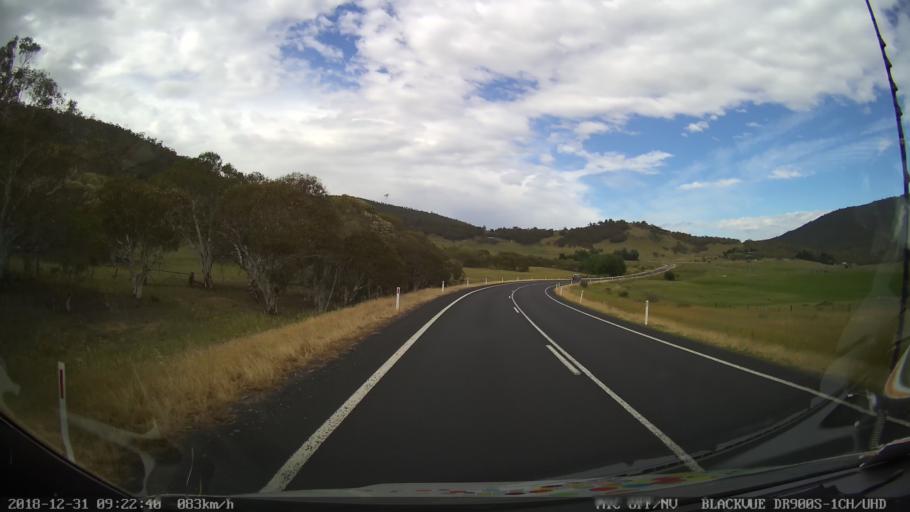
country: AU
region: New South Wales
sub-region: Snowy River
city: Jindabyne
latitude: -36.4357
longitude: 148.5444
